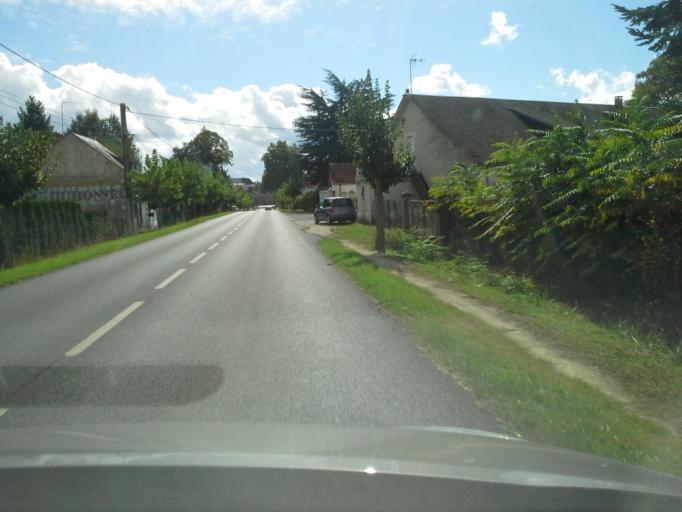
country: FR
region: Centre
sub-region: Departement du Loir-et-Cher
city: Les Montils
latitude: 47.4414
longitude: 1.2960
